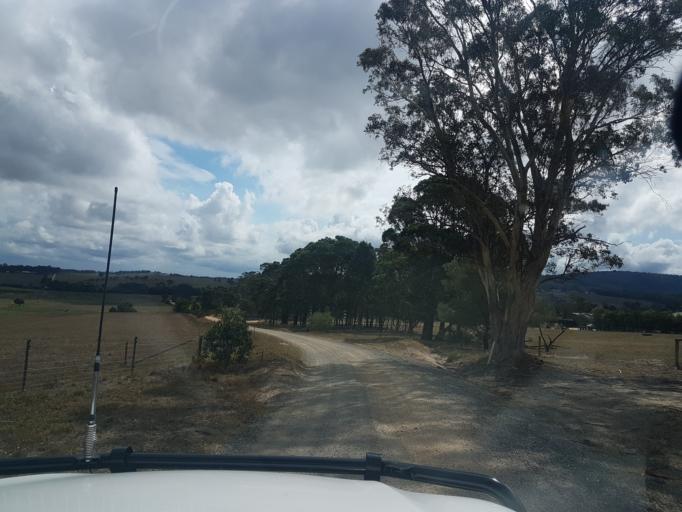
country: AU
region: Victoria
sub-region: East Gippsland
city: Bairnsdale
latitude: -37.7871
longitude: 147.5610
